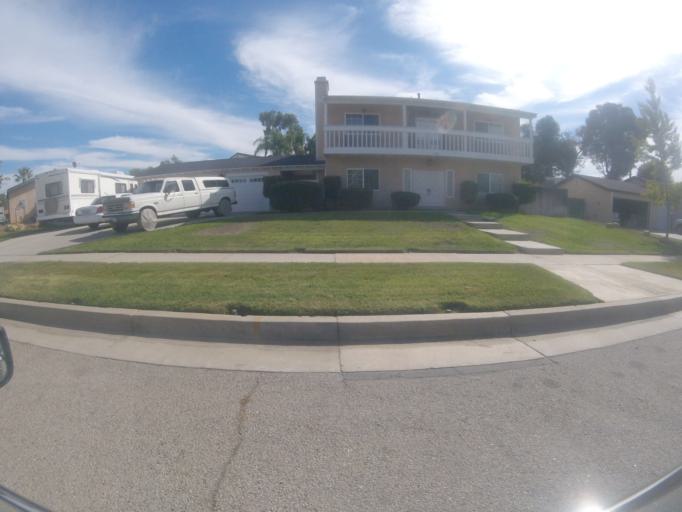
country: US
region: California
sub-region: San Bernardino County
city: Redlands
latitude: 34.0528
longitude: -117.1571
